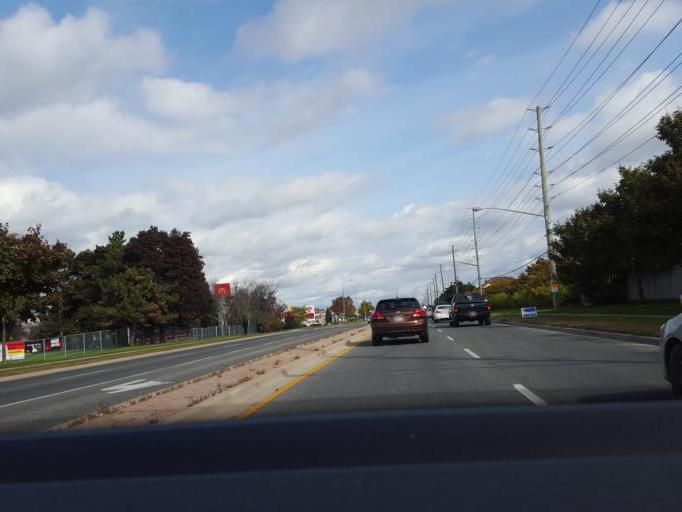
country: CA
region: Ontario
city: Oshawa
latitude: 43.9165
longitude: -78.9520
